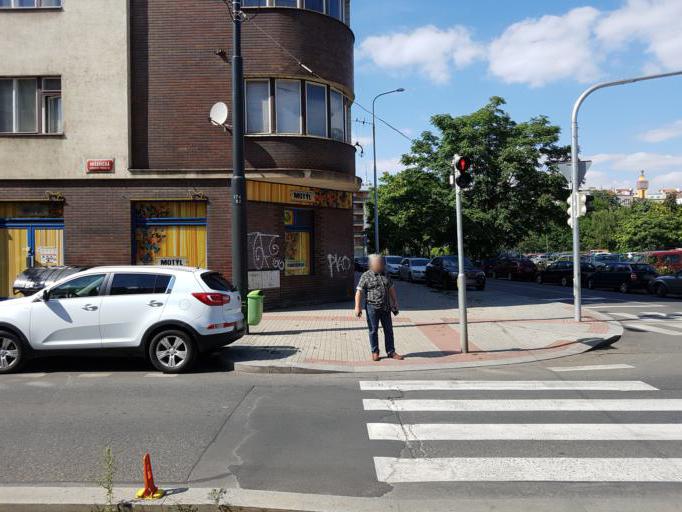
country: CZ
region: Praha
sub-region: Praha 8
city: Karlin
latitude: 50.0660
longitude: 14.4520
